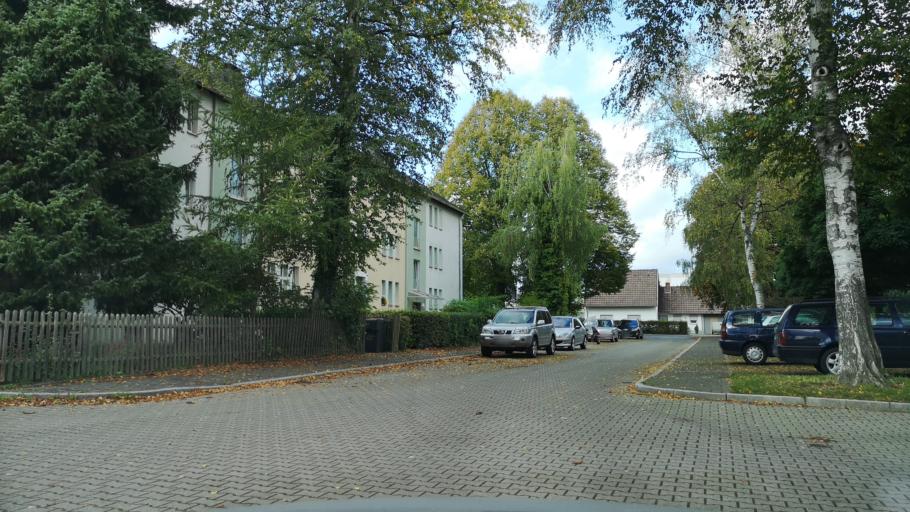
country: DE
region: North Rhine-Westphalia
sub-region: Regierungsbezirk Arnsberg
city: Menden
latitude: 51.4350
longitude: 7.7581
